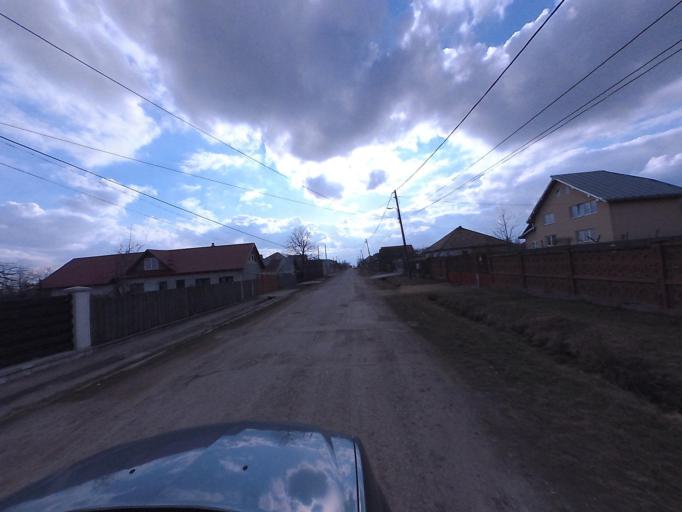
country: RO
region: Neamt
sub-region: Oras Targu Neamt
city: Targu Neamt
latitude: 47.2145
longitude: 26.3803
